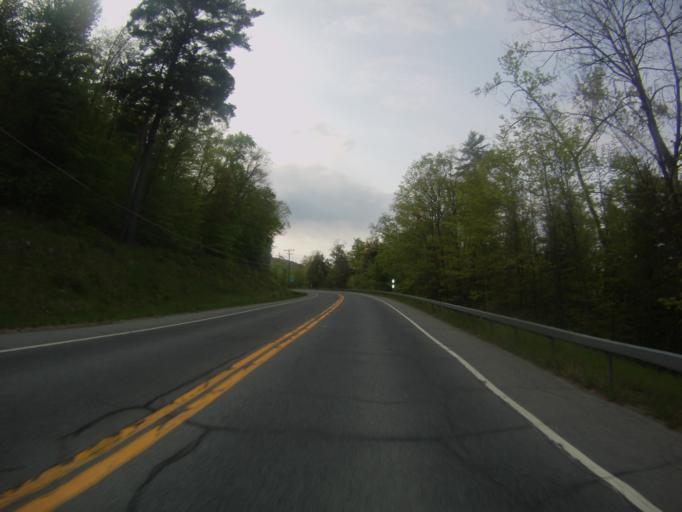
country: US
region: New York
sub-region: Essex County
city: Ticonderoga
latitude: 43.7583
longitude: -73.4857
